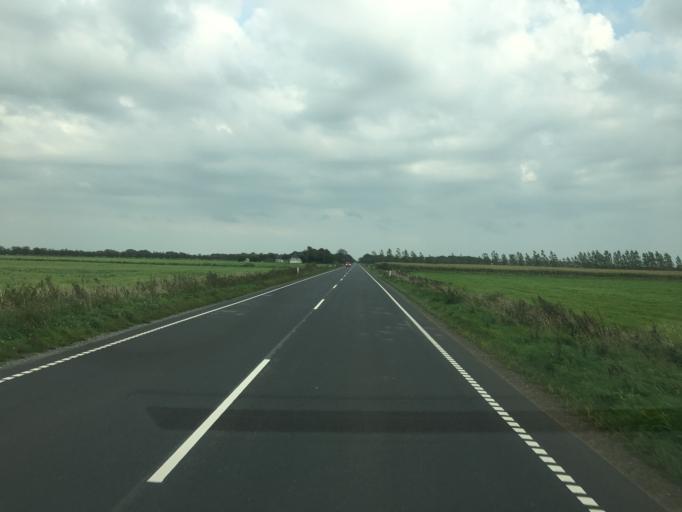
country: DK
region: South Denmark
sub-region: Tonder Kommune
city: Logumkloster
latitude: 54.9811
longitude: 9.0234
